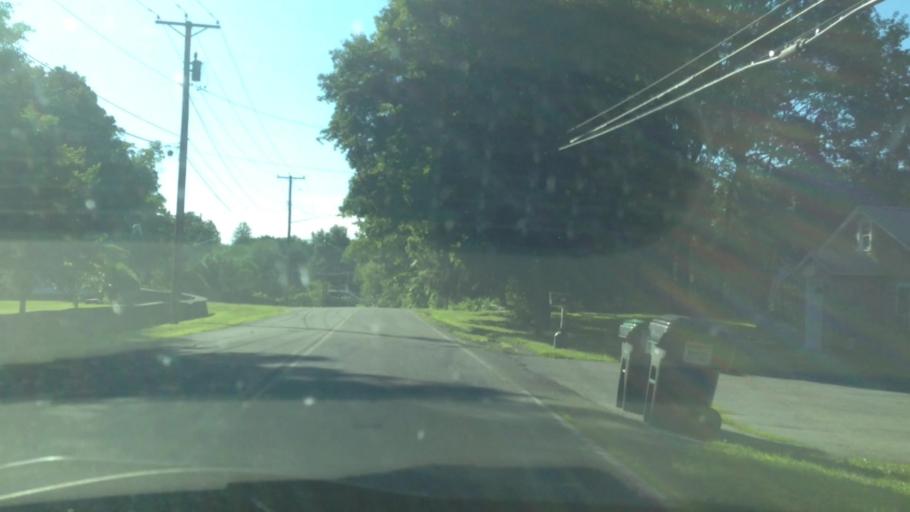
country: US
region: New York
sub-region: Ulster County
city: Clintondale
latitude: 41.7417
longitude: -74.0384
